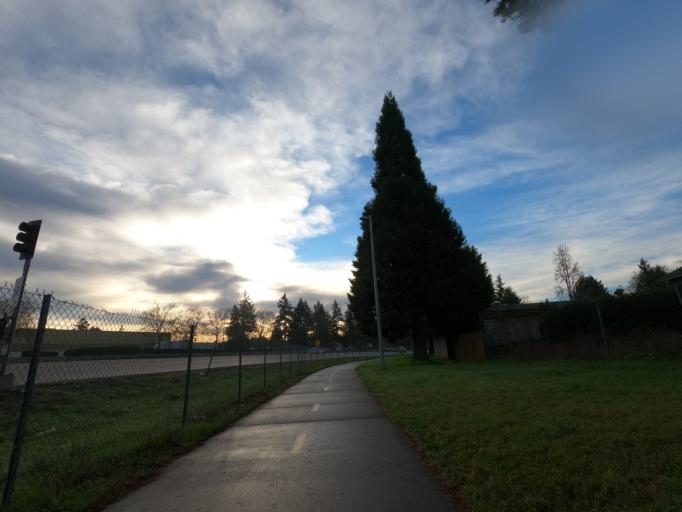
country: US
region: Oregon
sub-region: Clackamas County
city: Clackamas
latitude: 45.4045
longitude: -122.5723
